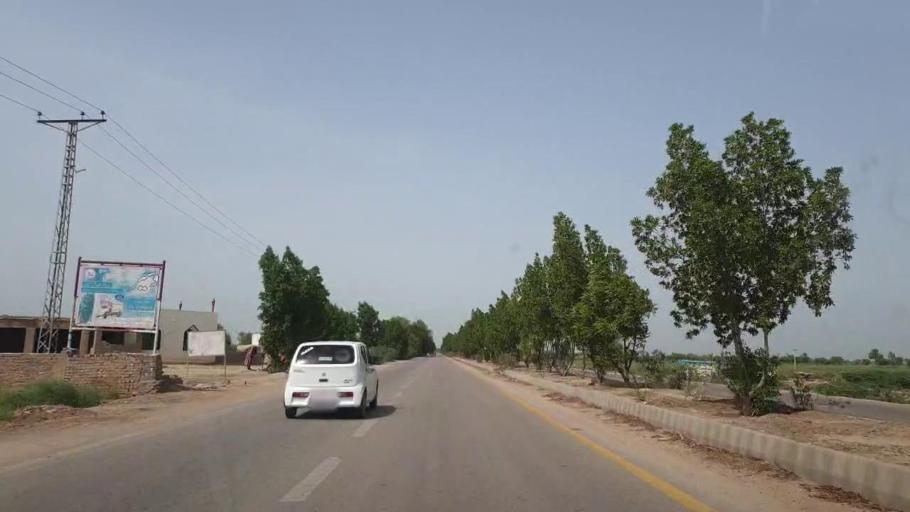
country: PK
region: Sindh
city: Sakrand
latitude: 26.1637
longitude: 68.2787
